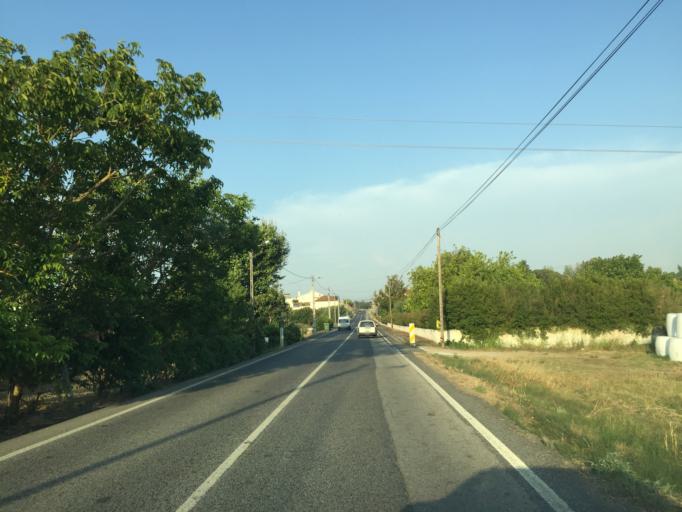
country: PT
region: Santarem
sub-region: Tomar
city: Tomar
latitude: 39.5505
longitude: -8.3829
